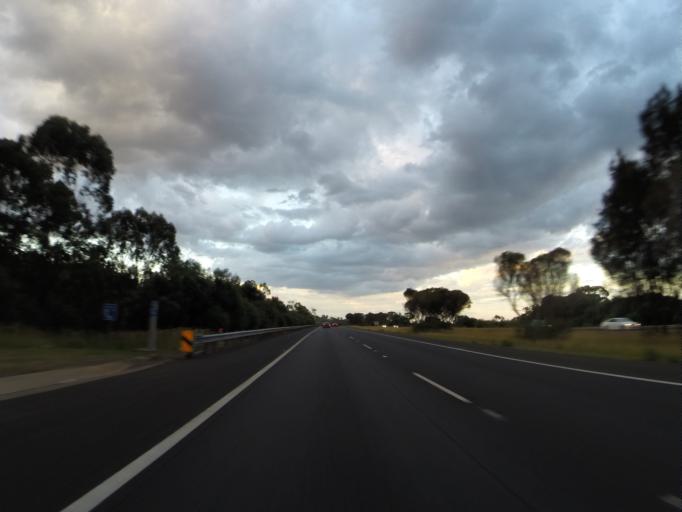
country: AU
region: New South Wales
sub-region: Campbelltown Municipality
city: Glen Alpine
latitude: -34.0742
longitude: 150.7759
